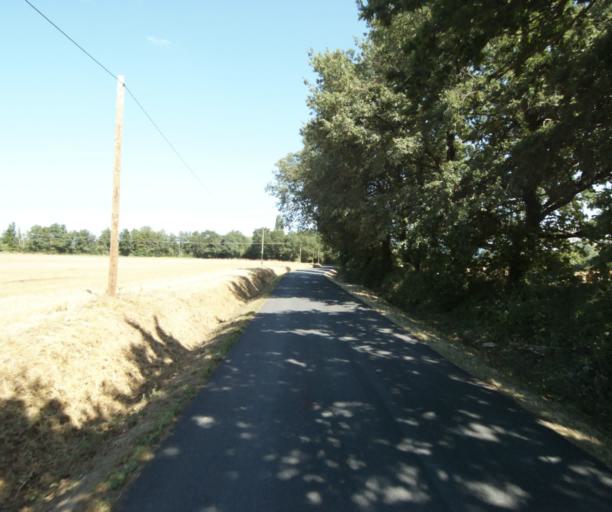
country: FR
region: Midi-Pyrenees
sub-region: Departement de la Haute-Garonne
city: Revel
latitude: 43.4747
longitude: 1.9949
